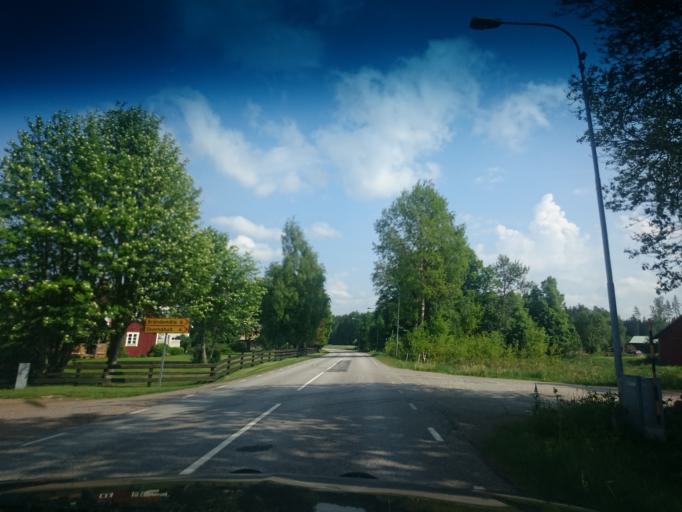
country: SE
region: Joenkoeping
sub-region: Vetlanda Kommun
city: Vetlanda
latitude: 57.3760
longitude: 15.0428
